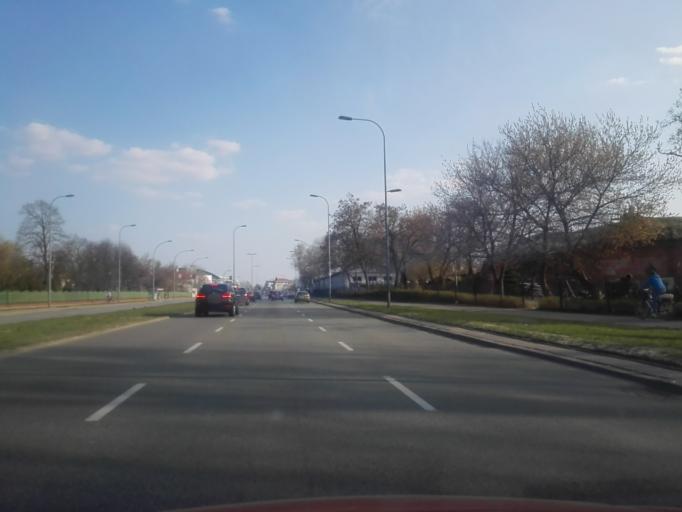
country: PL
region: Masovian Voivodeship
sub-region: Warszawa
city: Wilanow
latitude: 52.1837
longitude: 21.0671
